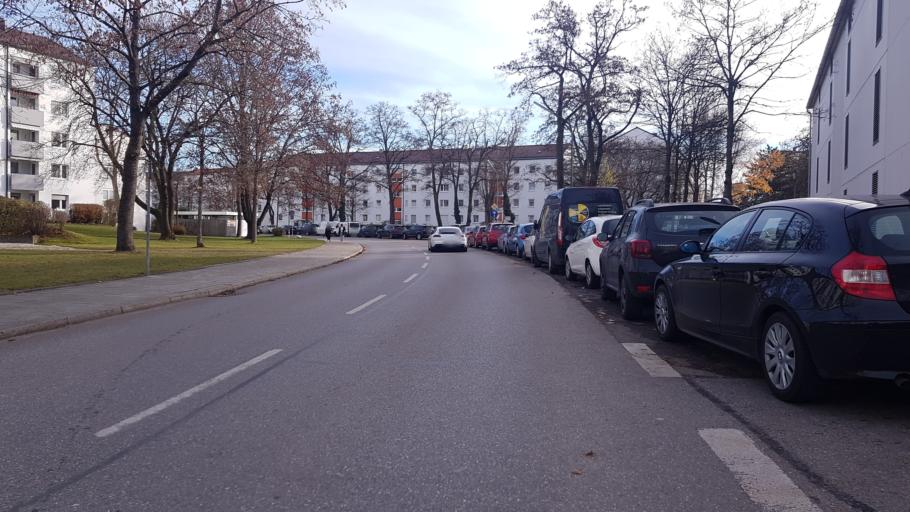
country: DE
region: Bavaria
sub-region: Upper Bavaria
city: Oberschleissheim
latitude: 48.2155
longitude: 11.5535
